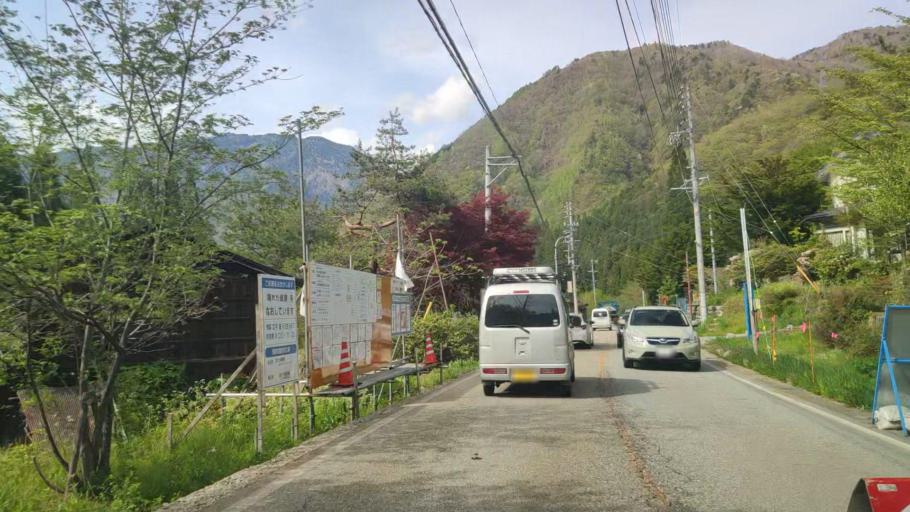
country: JP
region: Gifu
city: Takayama
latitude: 36.2295
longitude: 137.5327
